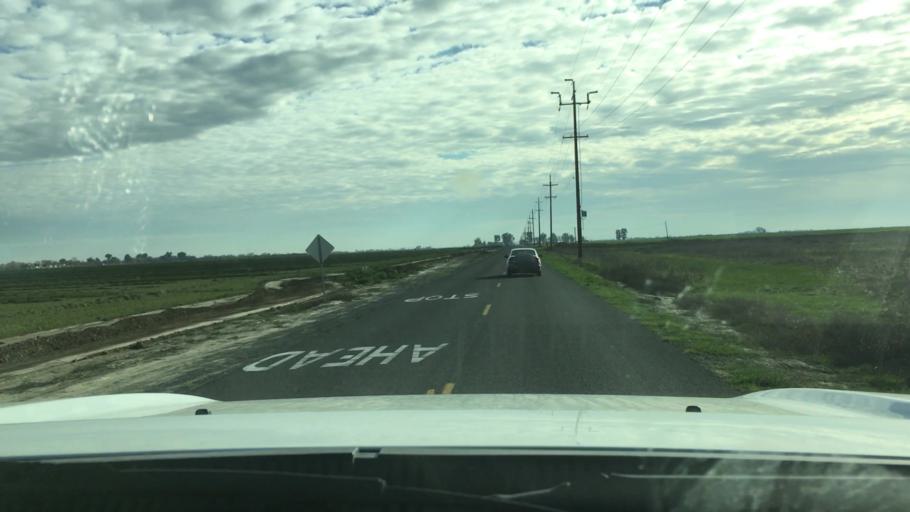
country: US
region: California
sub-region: Kings County
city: Stratford
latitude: 36.2259
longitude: -119.7788
